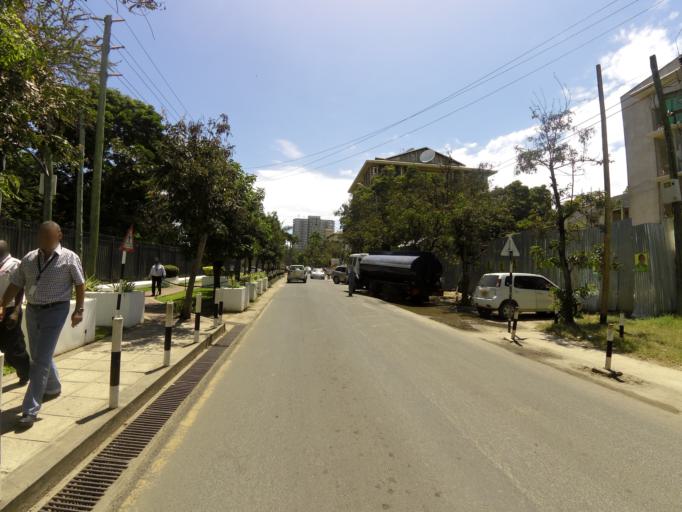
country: TZ
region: Dar es Salaam
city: Dar es Salaam
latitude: -6.8126
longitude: 39.2919
